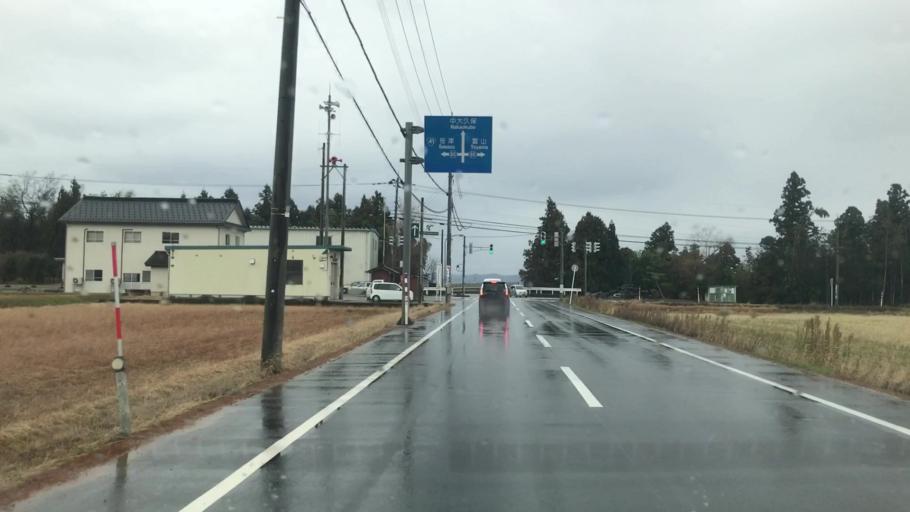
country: JP
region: Toyama
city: Toyama-shi
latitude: 36.6031
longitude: 137.2298
